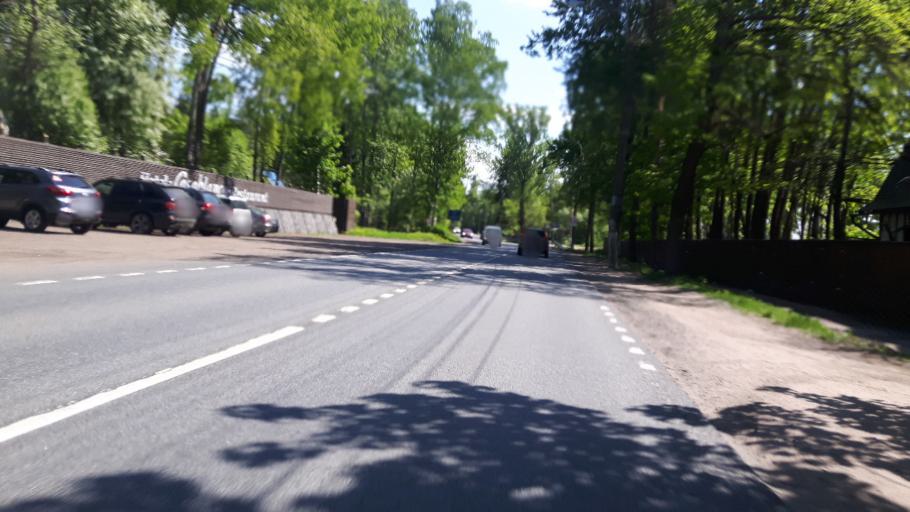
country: RU
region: St.-Petersburg
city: Komarovo
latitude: 60.1679
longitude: 29.8246
